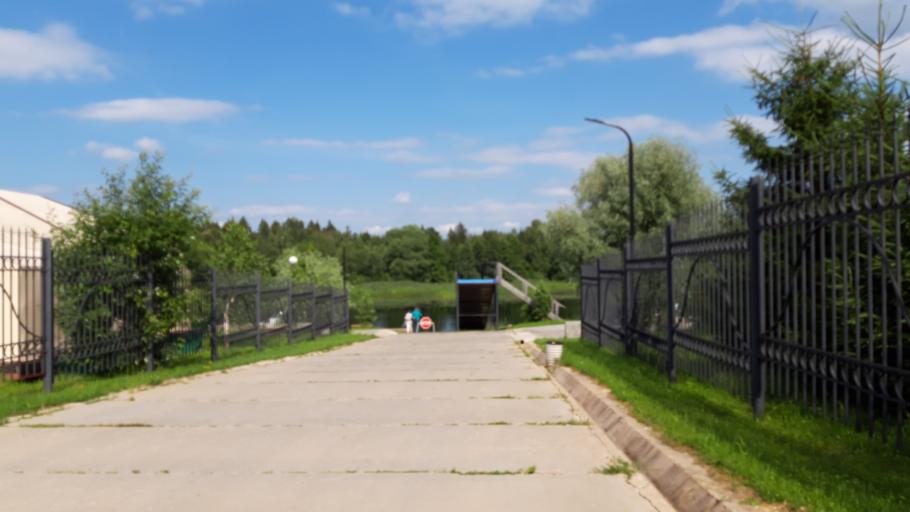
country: RU
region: Tverskaya
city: Konakovo
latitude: 56.6780
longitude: 36.7198
